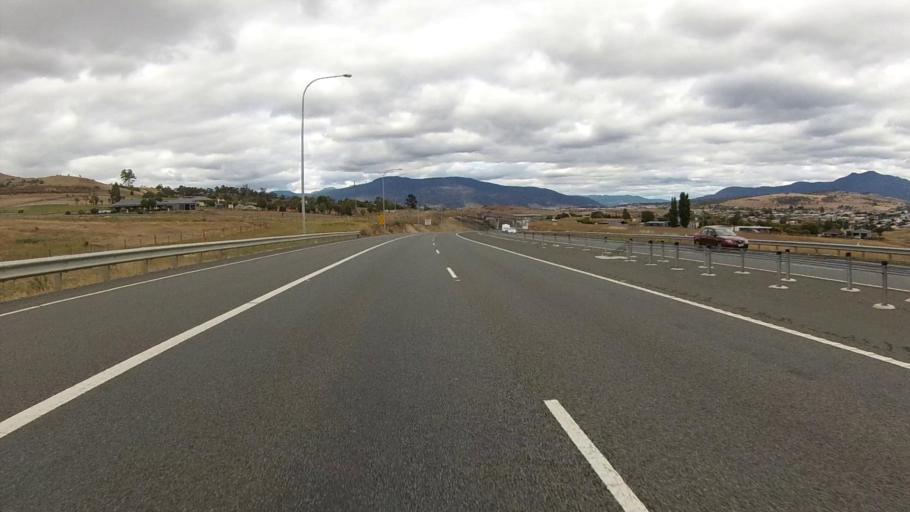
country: AU
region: Tasmania
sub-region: Brighton
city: Bridgewater
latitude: -42.7005
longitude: 147.2747
